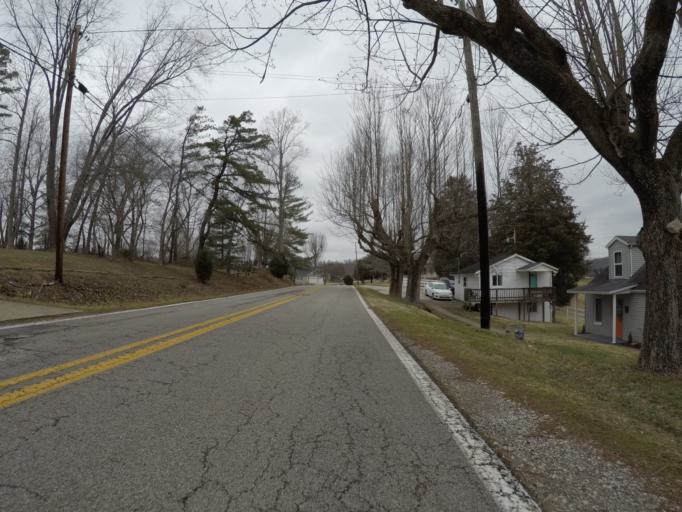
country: US
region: West Virginia
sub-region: Cabell County
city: Barboursville
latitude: 38.4316
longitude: -82.2428
